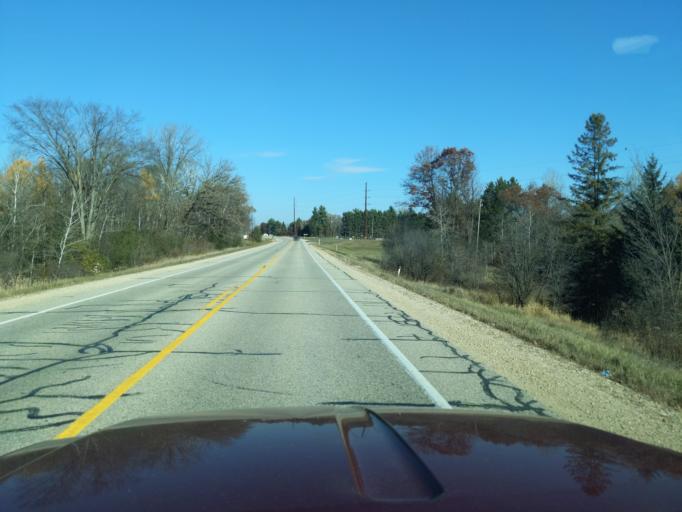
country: US
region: Wisconsin
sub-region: Waushara County
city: Wautoma
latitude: 44.0520
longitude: -89.2936
